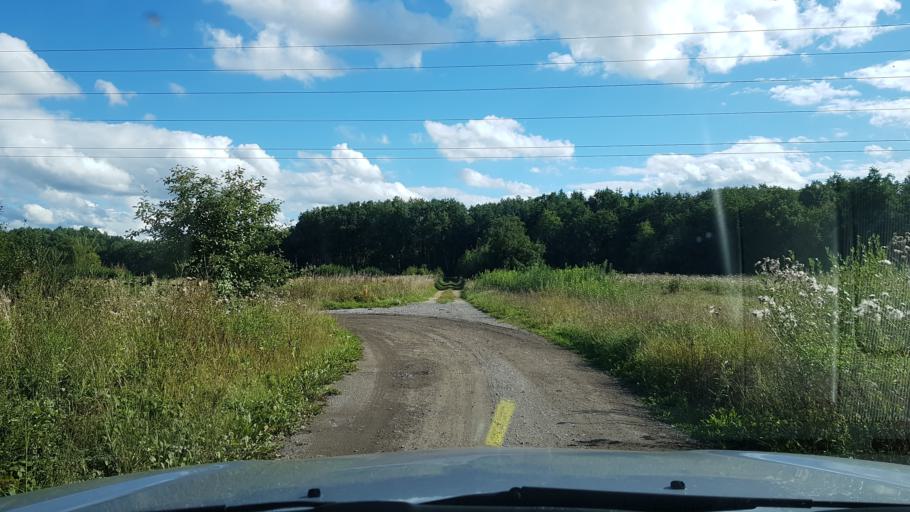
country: EE
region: Harju
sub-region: Rae vald
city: Jueri
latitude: 59.3689
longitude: 24.8387
